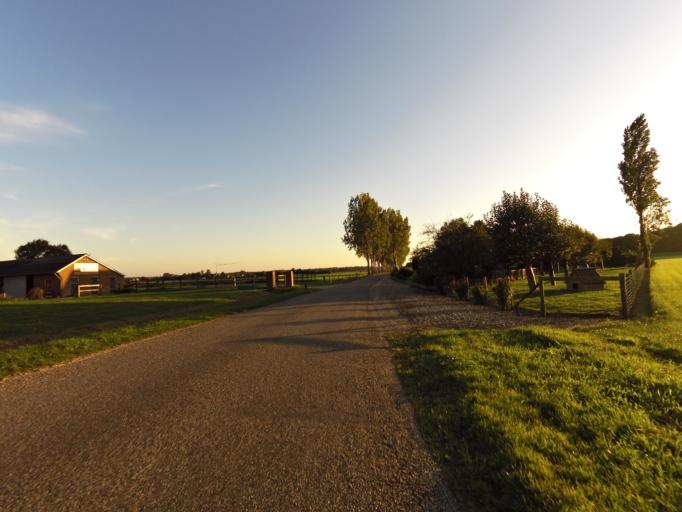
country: NL
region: Gelderland
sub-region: Gemeente Doesburg
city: Doesburg
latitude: 51.9271
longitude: 6.1603
